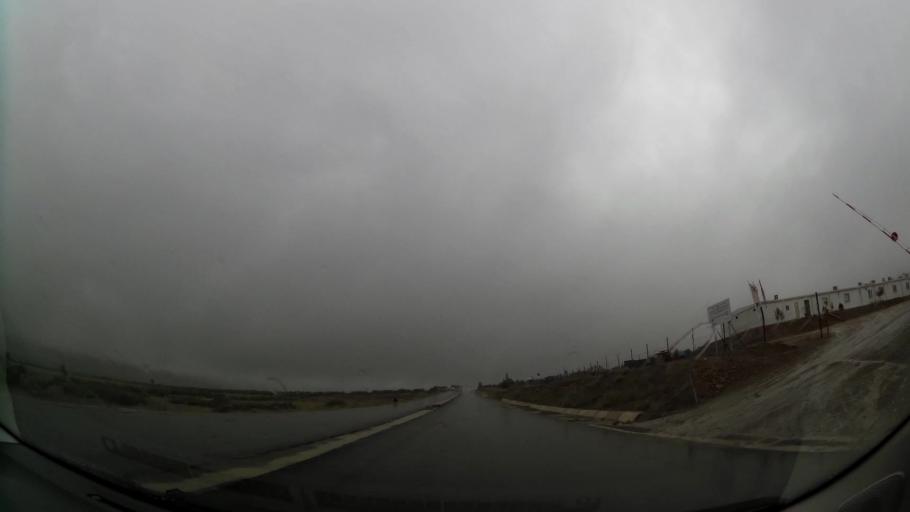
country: MA
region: Oriental
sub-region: Nador
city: Midar
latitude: 34.8642
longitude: -3.7240
